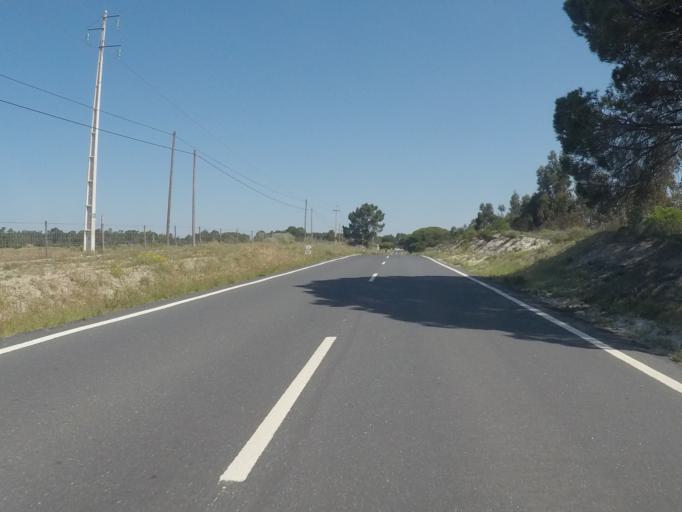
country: PT
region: Setubal
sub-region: Grandola
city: Grandola
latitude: 38.2505
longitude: -8.7375
